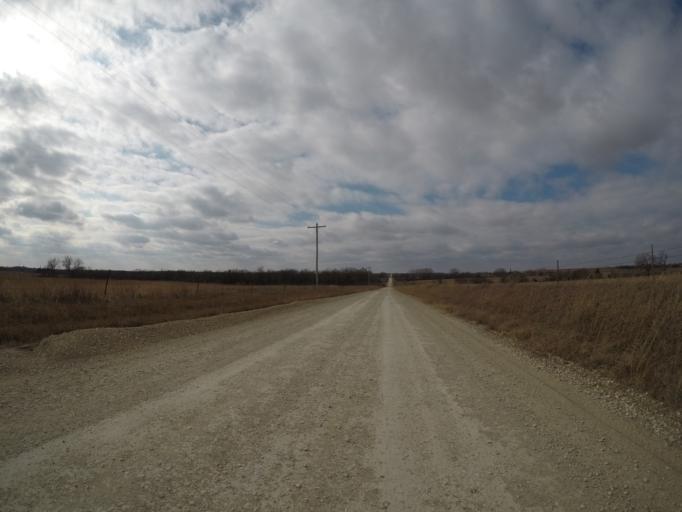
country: US
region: Kansas
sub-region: Morris County
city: Council Grove
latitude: 38.7681
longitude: -96.3419
